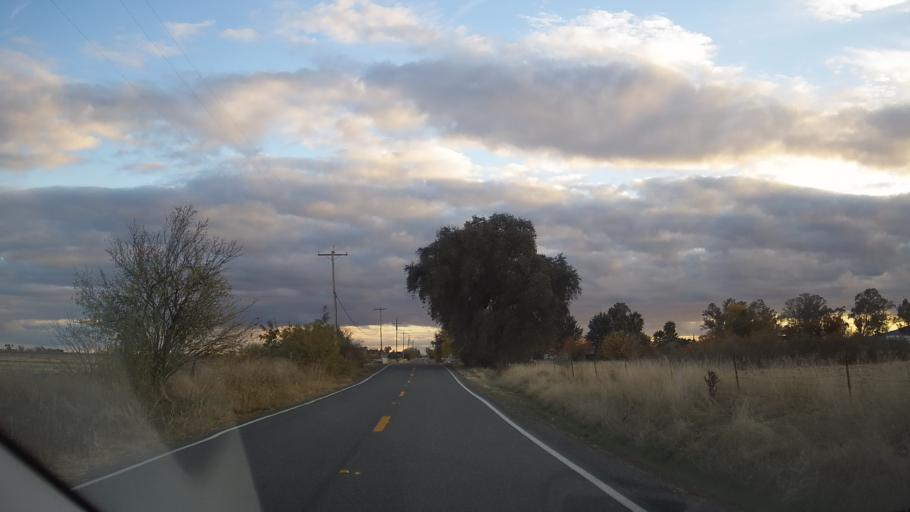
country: US
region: California
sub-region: Solano County
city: Hartley
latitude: 38.4004
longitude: -121.9062
